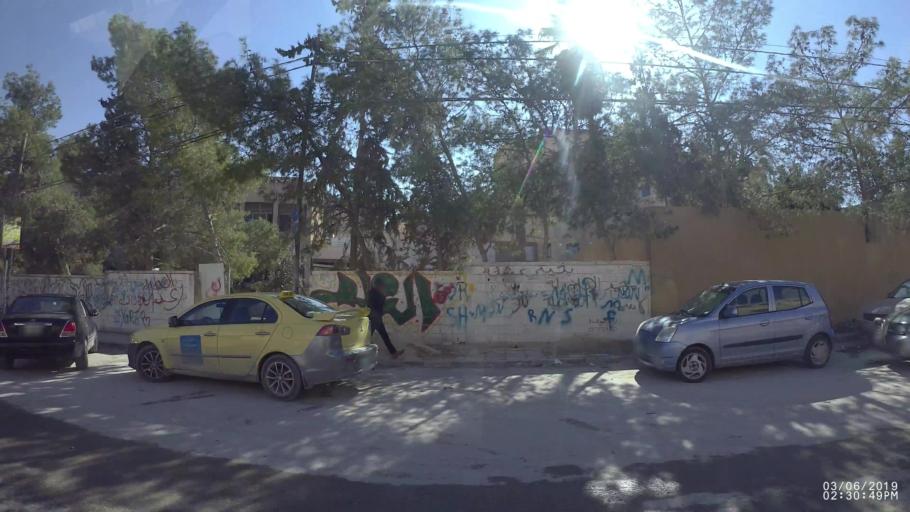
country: JO
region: Zarqa
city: Russeifa
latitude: 32.0322
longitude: 36.0390
